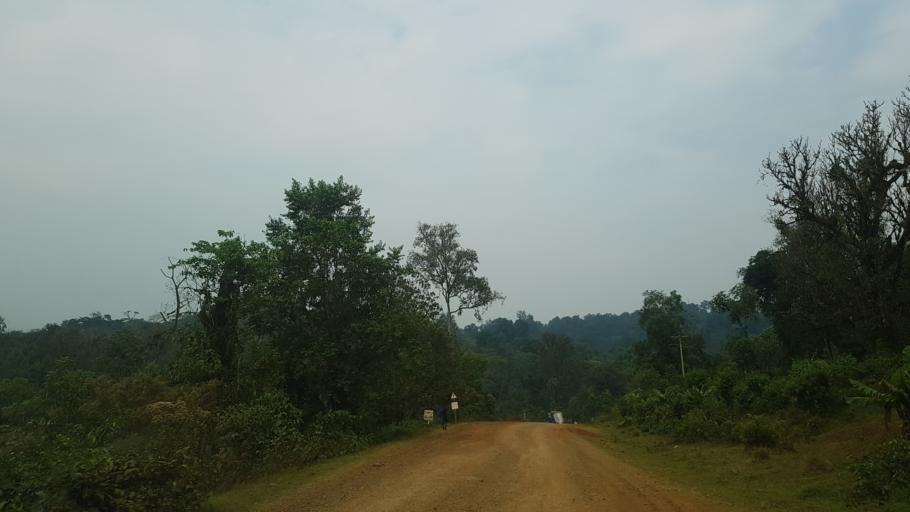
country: ET
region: Oromiya
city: Gore
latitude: 7.8755
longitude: 35.4804
